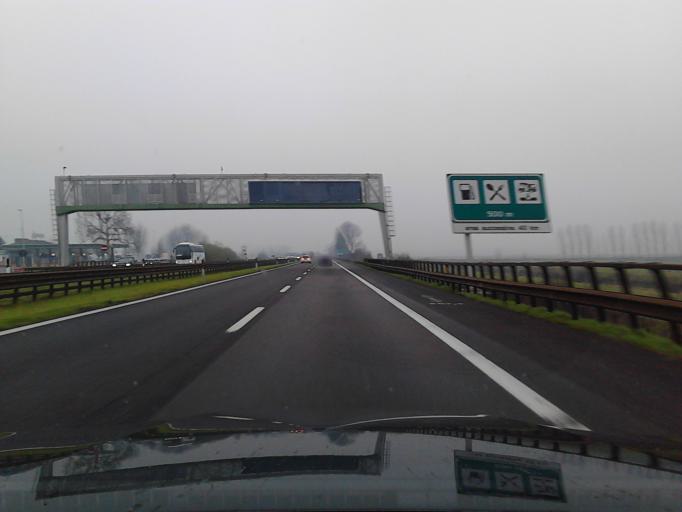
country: IT
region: Lombardy
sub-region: Provincia di Mantova
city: San Biagio
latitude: 45.0684
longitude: 10.8441
